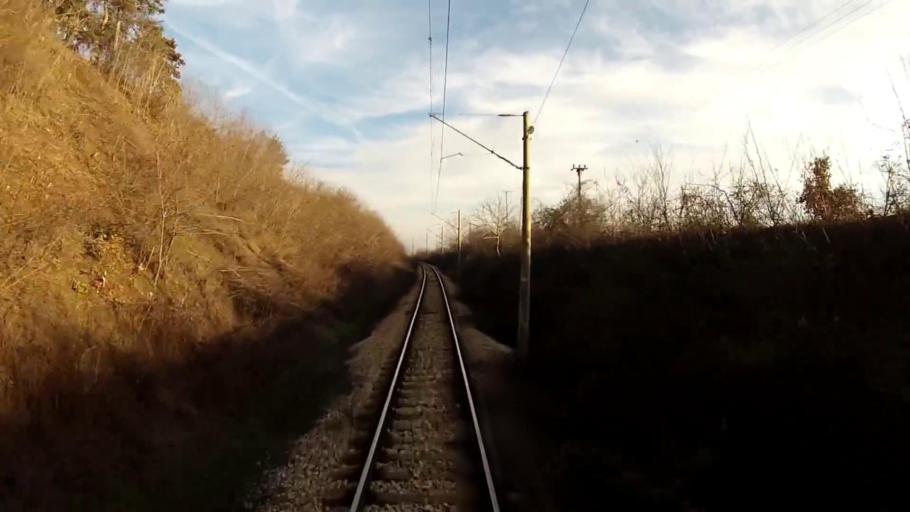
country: BG
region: Plovdiv
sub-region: Obshtina Karlovo
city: Klisura
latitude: 42.7175
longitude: 24.5990
